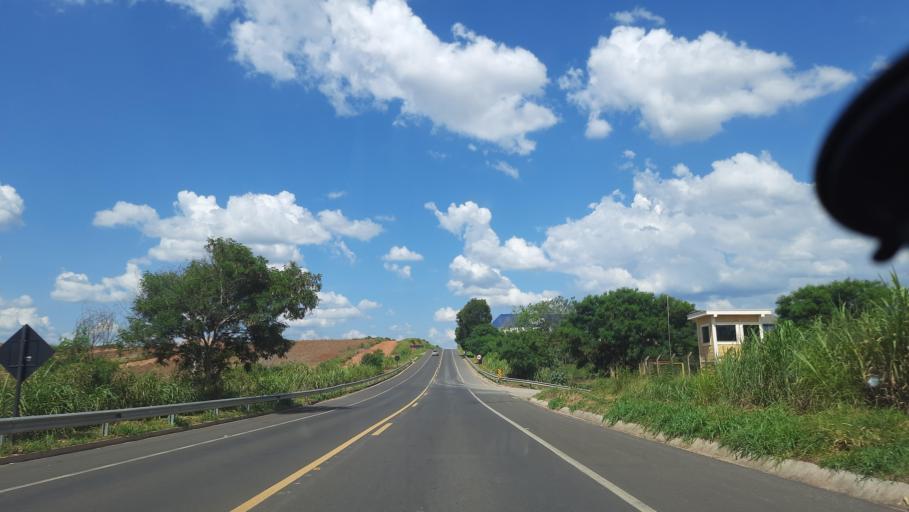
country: BR
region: Sao Paulo
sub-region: Sao Jose Do Rio Pardo
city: Sao Jose do Rio Pardo
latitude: -21.6033
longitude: -46.9241
